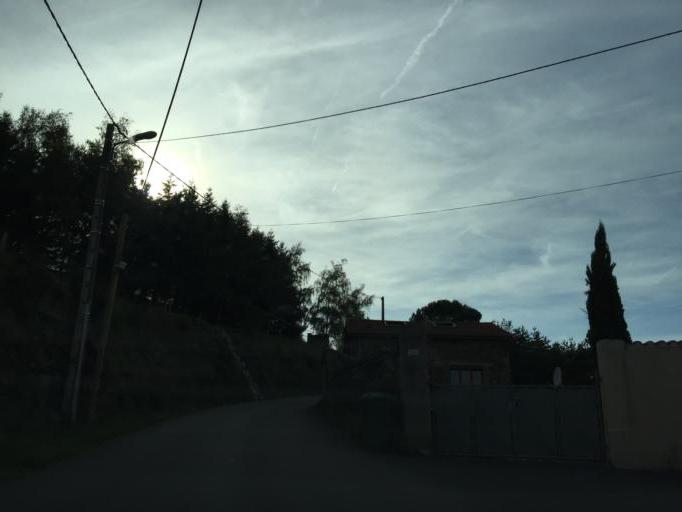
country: FR
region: Rhone-Alpes
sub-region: Departement de la Loire
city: Cellieu
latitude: 45.5313
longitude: 4.5561
